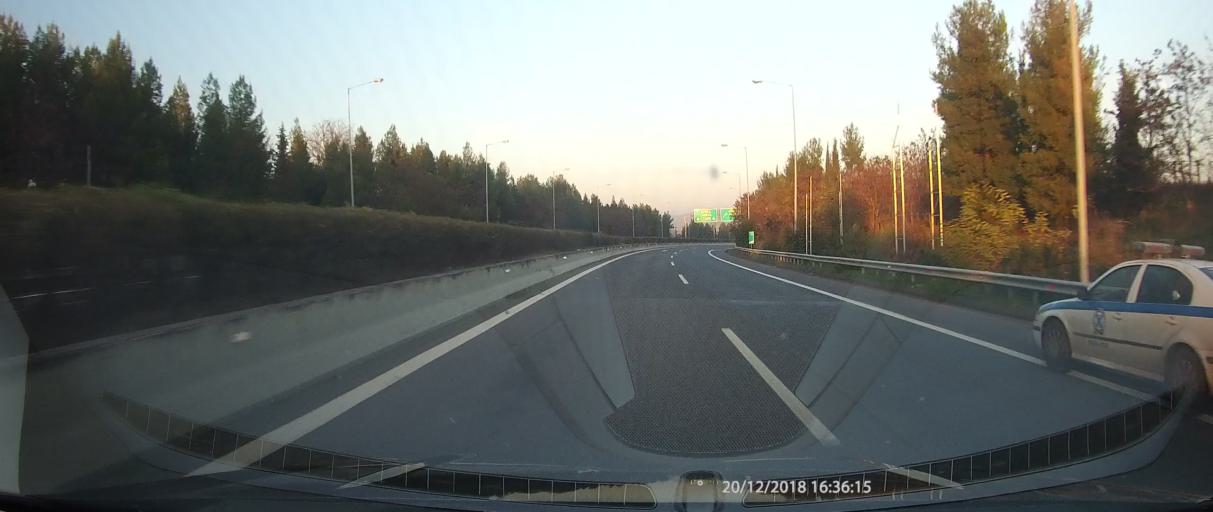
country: GR
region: Thessaly
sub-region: Nomos Magnisias
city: Velestino
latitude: 39.3163
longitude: 22.7530
